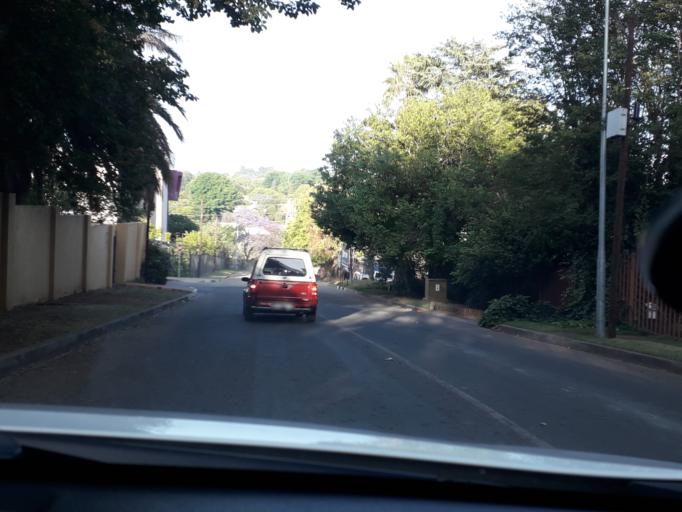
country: ZA
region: Gauteng
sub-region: City of Johannesburg Metropolitan Municipality
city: Johannesburg
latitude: -26.1243
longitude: 28.0734
